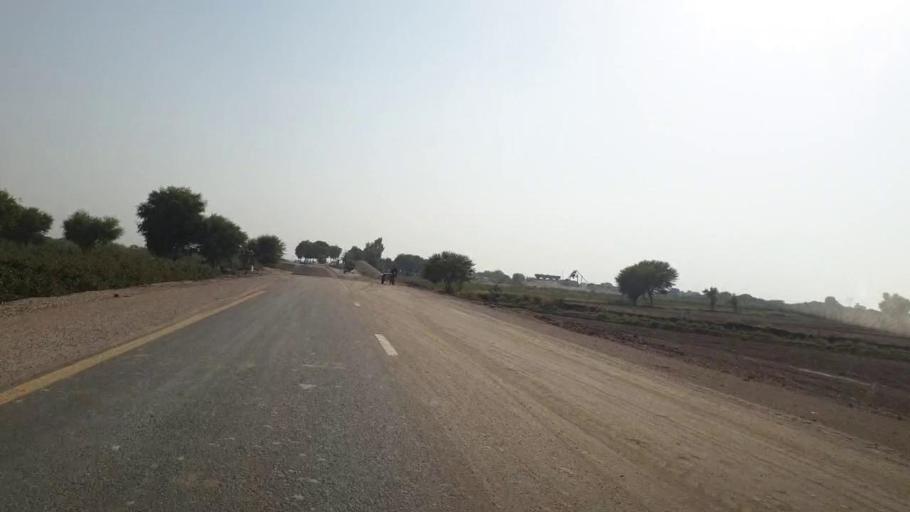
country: PK
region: Sindh
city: Bhan
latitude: 26.5040
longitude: 67.7828
